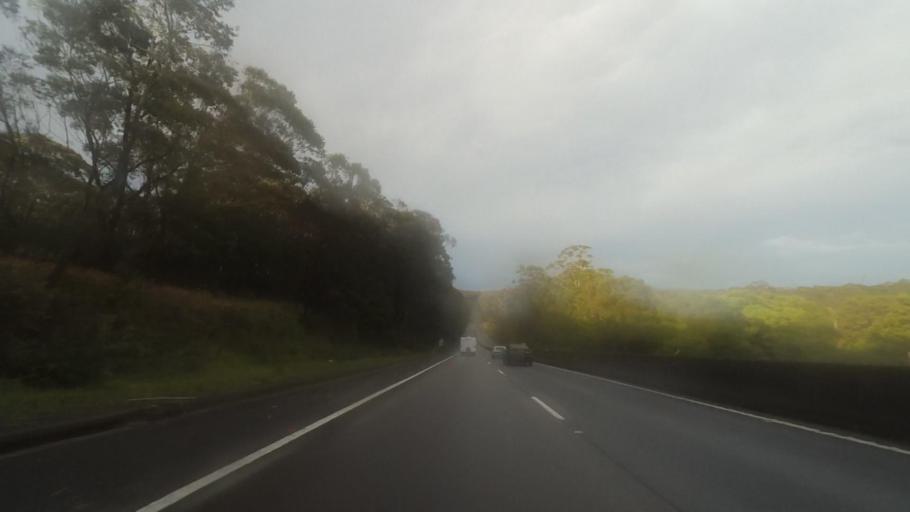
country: AU
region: New South Wales
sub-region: Wollongong
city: Corrimal
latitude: -34.3525
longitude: 150.8655
